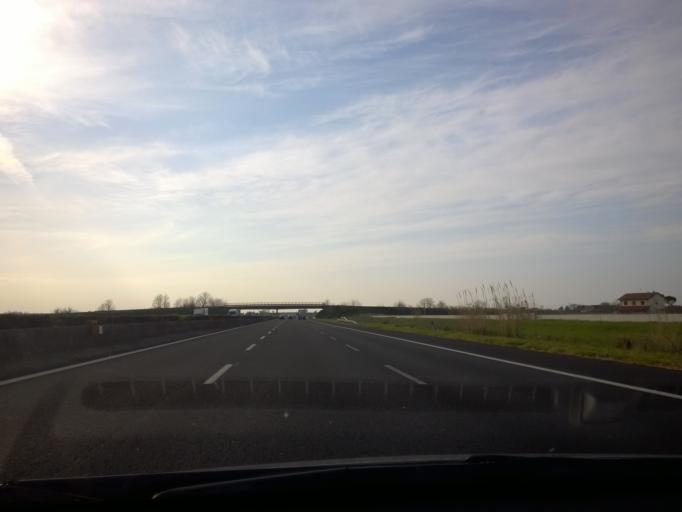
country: IT
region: Emilia-Romagna
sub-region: Forli-Cesena
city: Sala
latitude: 44.1350
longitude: 12.3647
